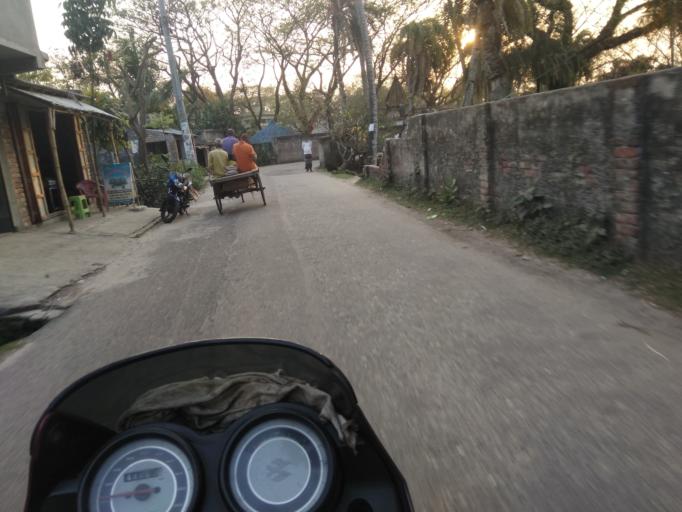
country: BD
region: Khulna
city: Satkhira
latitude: 22.5464
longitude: 89.1746
